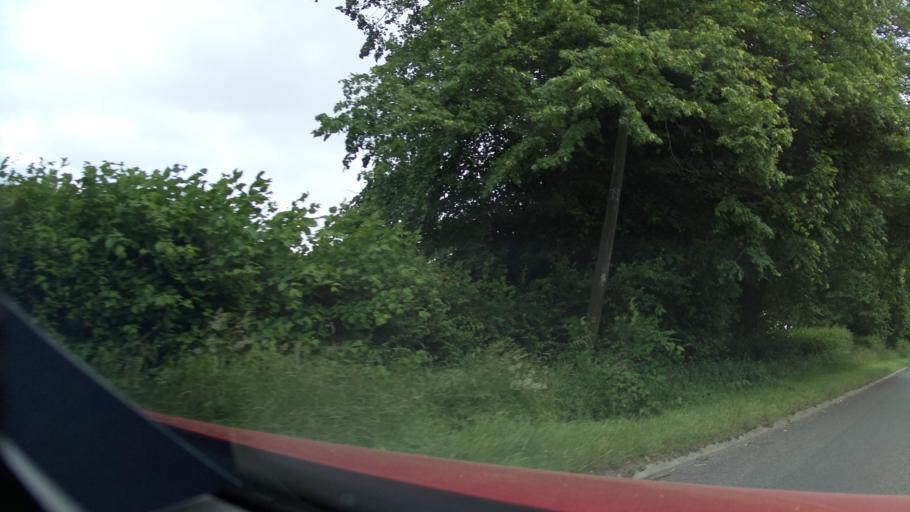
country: GB
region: Wales
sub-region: Vale of Glamorgan
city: Barry
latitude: 51.4631
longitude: -3.2969
